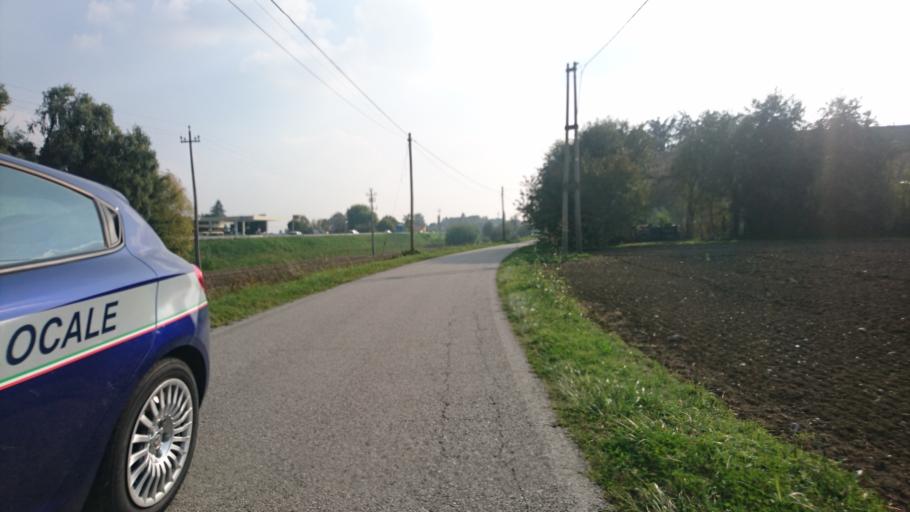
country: IT
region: Veneto
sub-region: Provincia di Rovigo
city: Polesella
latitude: 44.9748
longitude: 11.7551
